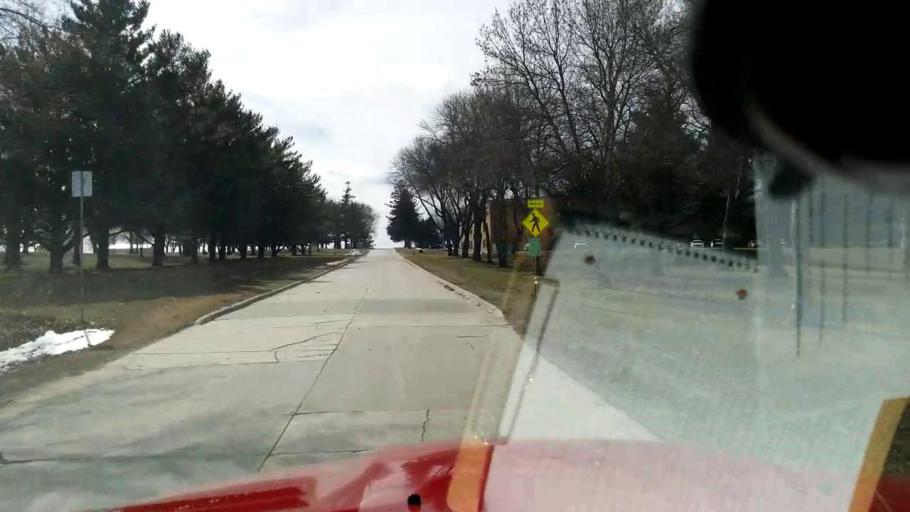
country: US
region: Iowa
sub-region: Buchanan County
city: Independence
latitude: 42.4542
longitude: -91.9230
